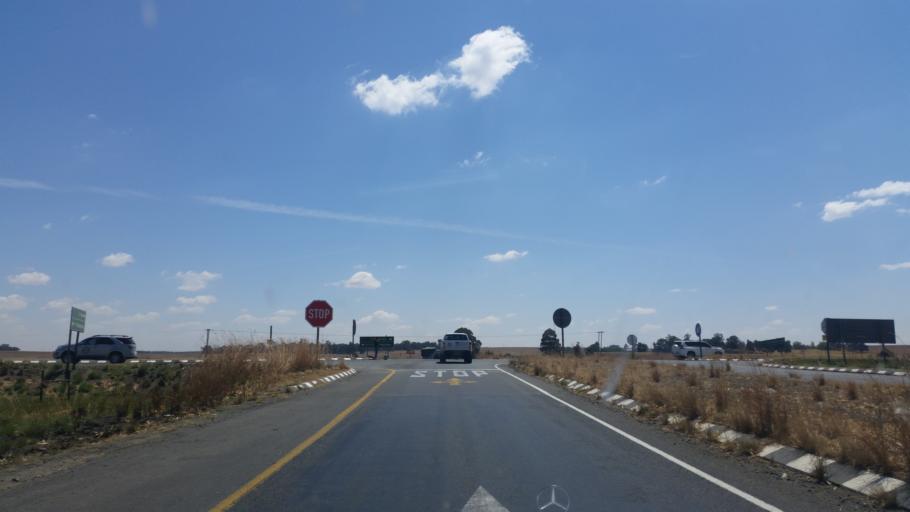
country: ZA
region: Orange Free State
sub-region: Thabo Mofutsanyana District Municipality
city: Reitz
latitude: -28.0837
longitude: 28.6496
